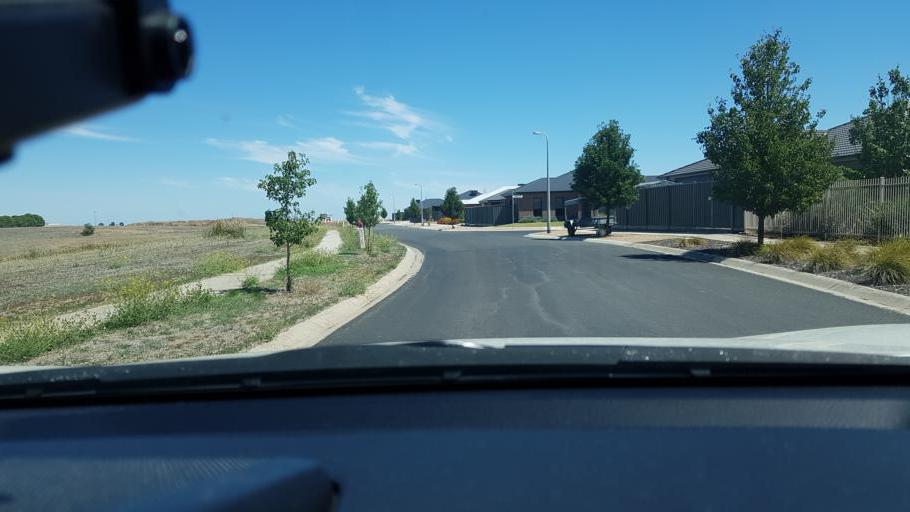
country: AU
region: Victoria
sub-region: Horsham
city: Horsham
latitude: -36.7156
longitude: 142.1785
